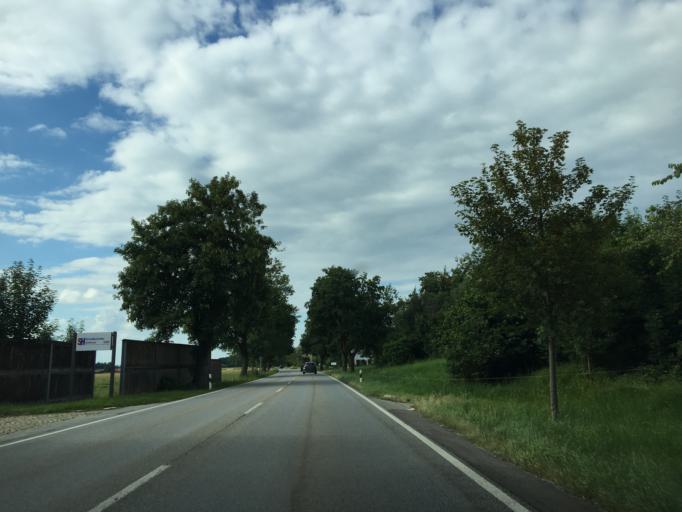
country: DE
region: Bavaria
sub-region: Upper Bavaria
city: Holzkirchen
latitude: 47.8620
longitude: 11.7188
